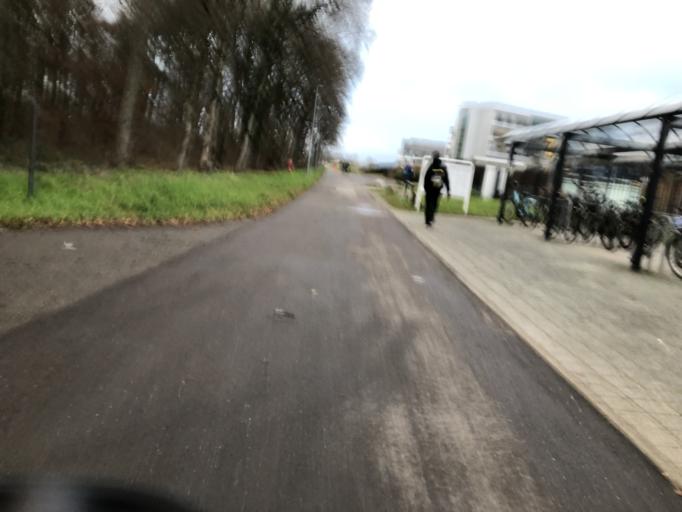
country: DE
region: Baden-Wuerttemberg
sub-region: Karlsruhe Region
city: Walldorf
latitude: 49.2928
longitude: 8.6372
